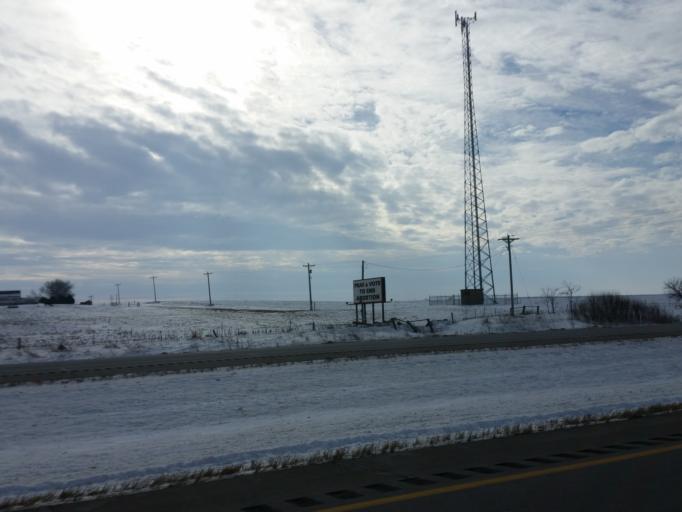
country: US
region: Iowa
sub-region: Delaware County
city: Manchester
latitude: 42.4636
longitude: -91.6556
